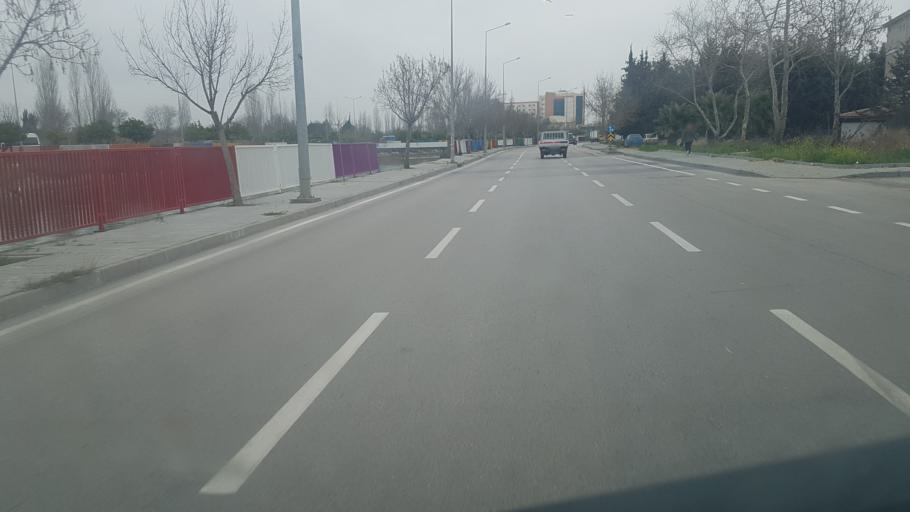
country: TR
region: Adana
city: Adana
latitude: 37.0127
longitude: 35.3474
